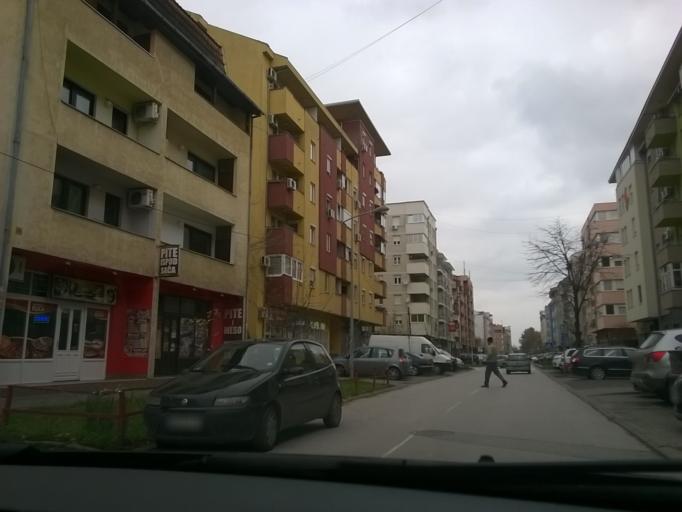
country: RS
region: Autonomna Pokrajina Vojvodina
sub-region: Juznobacki Okrug
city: Novi Sad
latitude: 45.2576
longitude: 19.8156
